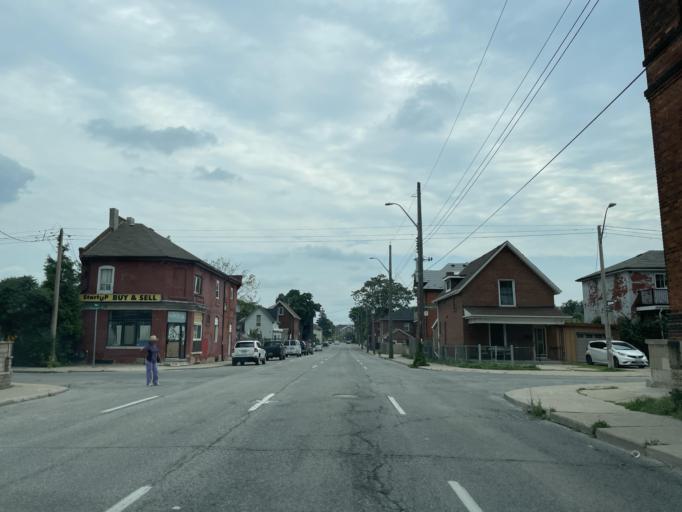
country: CA
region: Ontario
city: Hamilton
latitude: 43.2552
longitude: -79.8535
